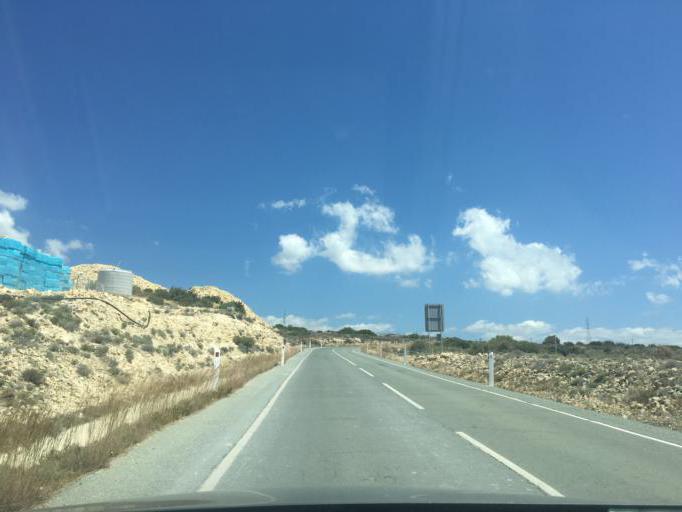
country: CY
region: Limassol
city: Mouttagiaka
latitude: 34.7300
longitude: 33.0616
